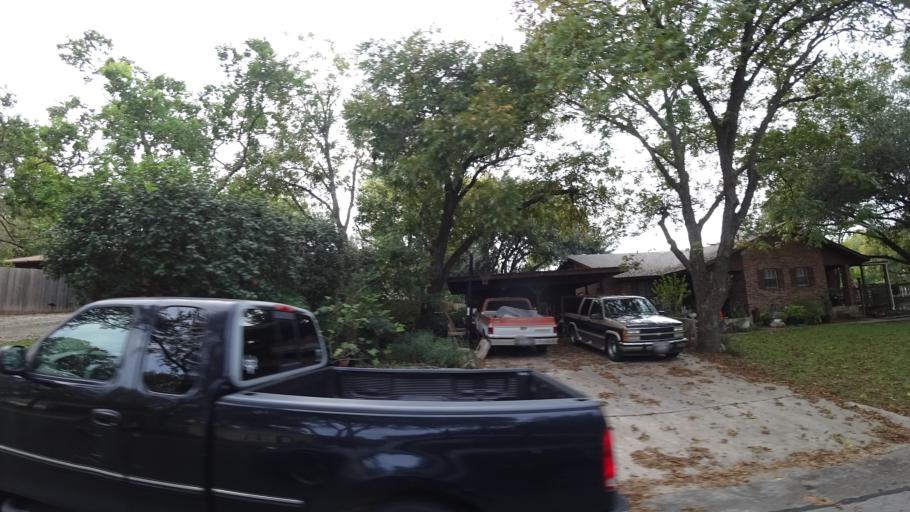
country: US
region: Texas
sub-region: Williamson County
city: Round Rock
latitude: 30.5137
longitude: -97.6694
